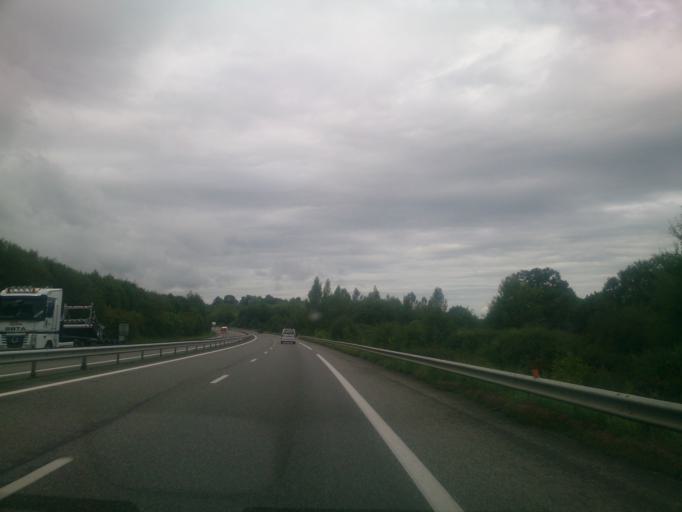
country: FR
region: Midi-Pyrenees
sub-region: Departement de la Haute-Garonne
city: Montrejeau
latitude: 43.0974
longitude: 0.5628
